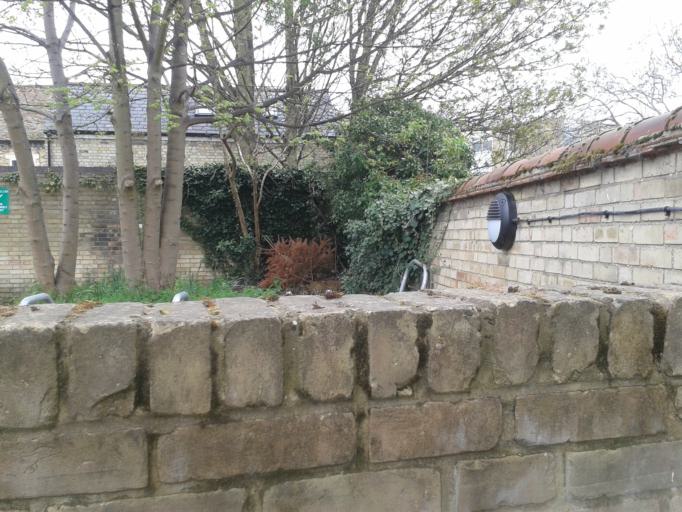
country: GB
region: England
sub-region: Cambridgeshire
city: Cambridge
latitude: 52.2173
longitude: 0.1395
